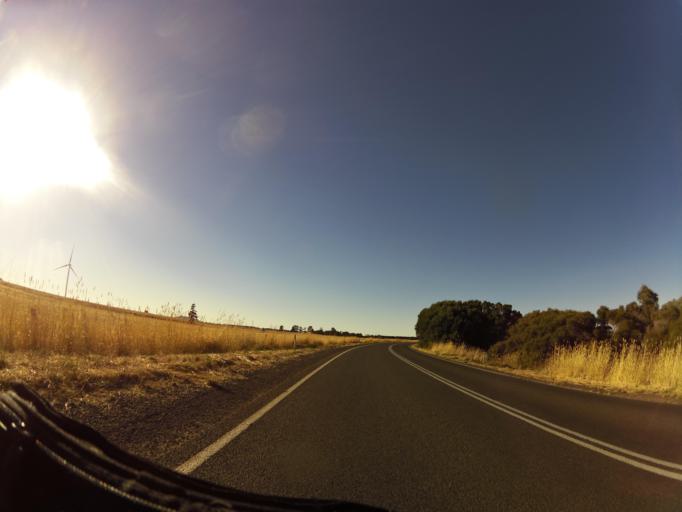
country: AU
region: Victoria
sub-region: Ballarat North
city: Delacombe
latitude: -37.5350
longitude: 143.3754
